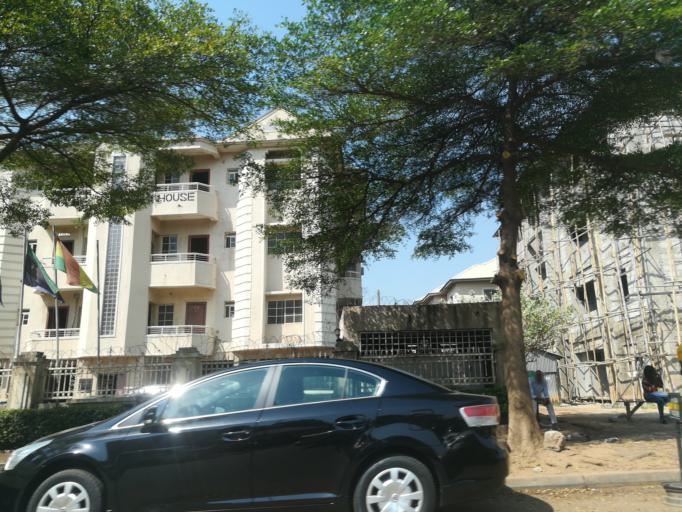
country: NG
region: Abuja Federal Capital Territory
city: Abuja
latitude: 9.0690
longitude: 7.4422
